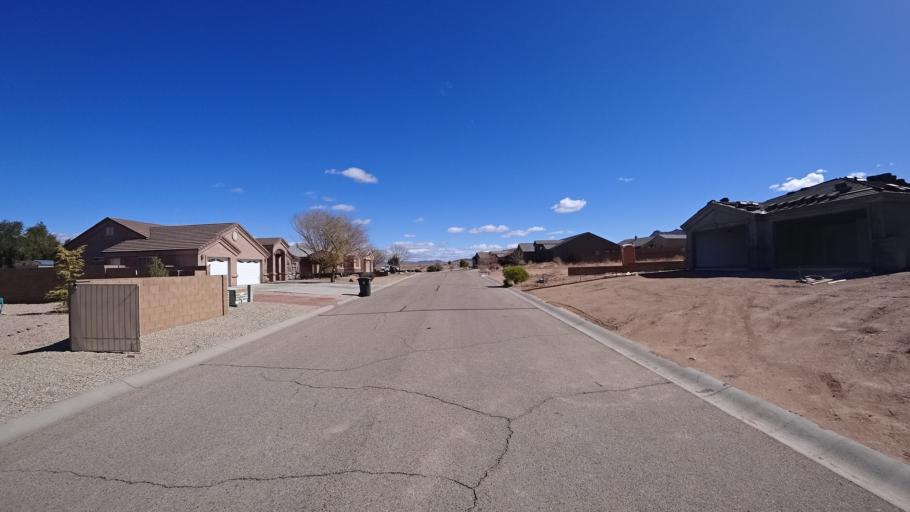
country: US
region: Arizona
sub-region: Mohave County
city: Kingman
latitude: 35.2053
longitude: -113.9691
